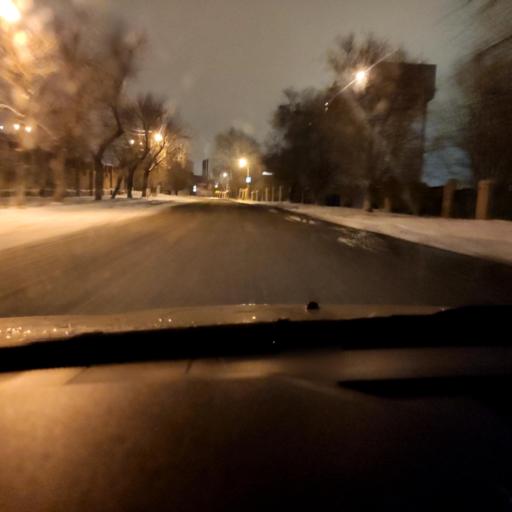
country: RU
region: Samara
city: Rozhdestveno
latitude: 53.1759
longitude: 50.0785
